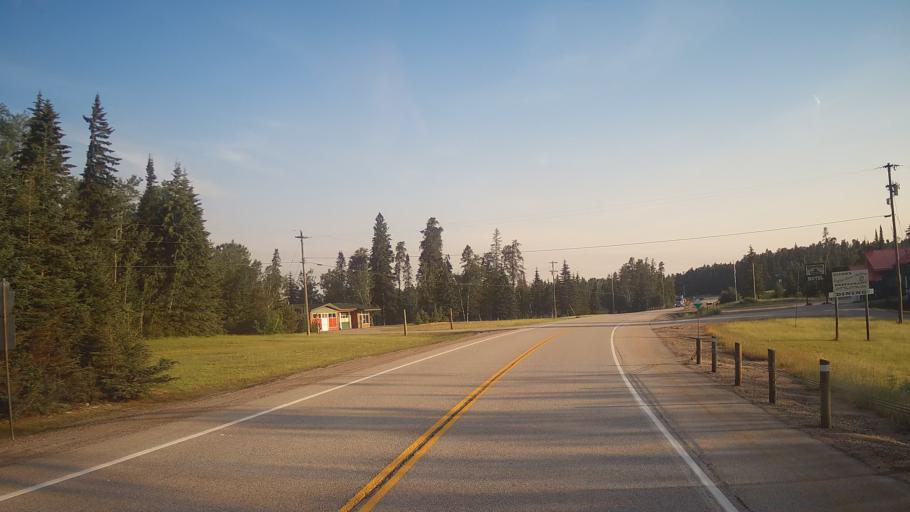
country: CA
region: Ontario
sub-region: Rainy River District
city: Atikokan
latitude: 49.2264
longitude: -90.9647
